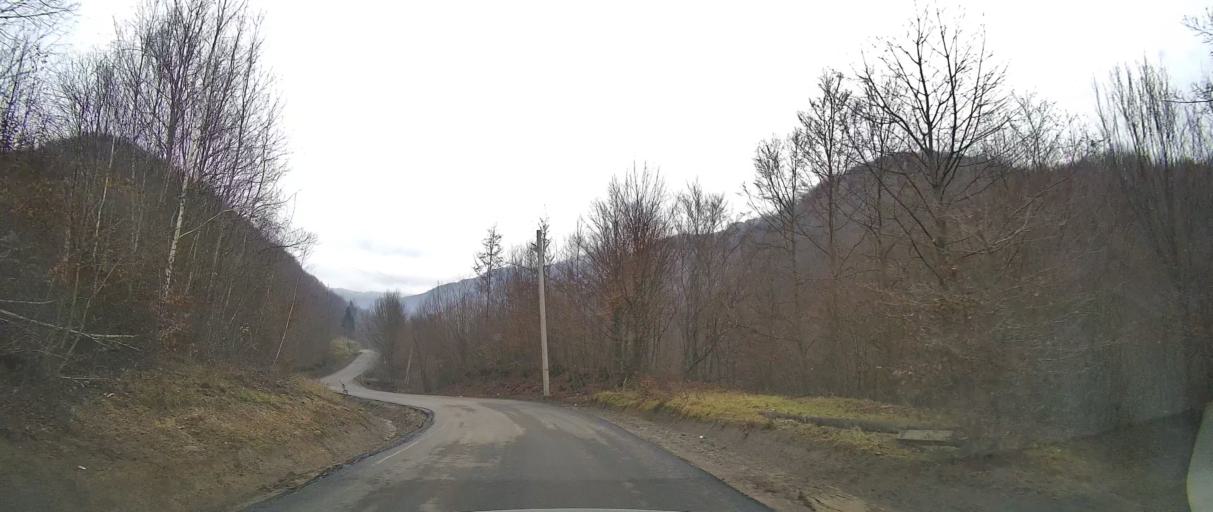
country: UA
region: Zakarpattia
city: Velykyi Bereznyi
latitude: 48.9559
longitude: 22.5463
